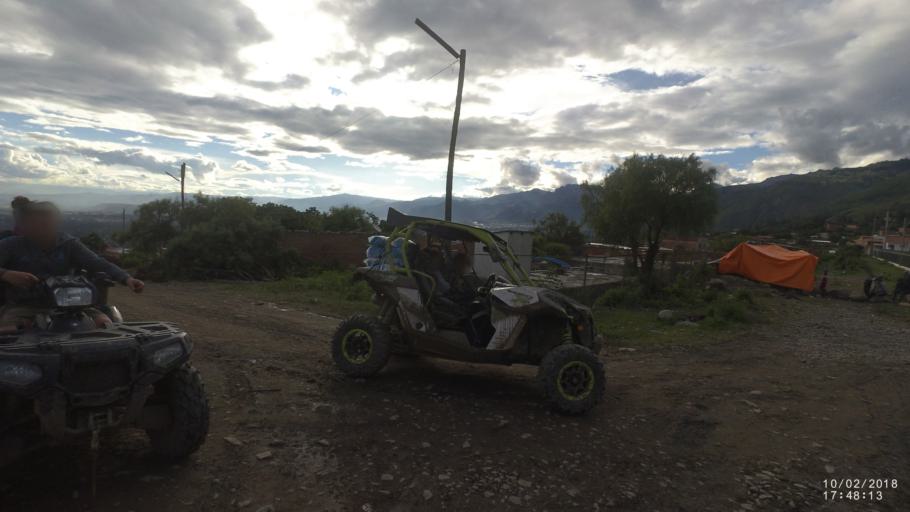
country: BO
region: Cochabamba
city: Cochabamba
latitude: -17.3396
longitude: -66.1990
